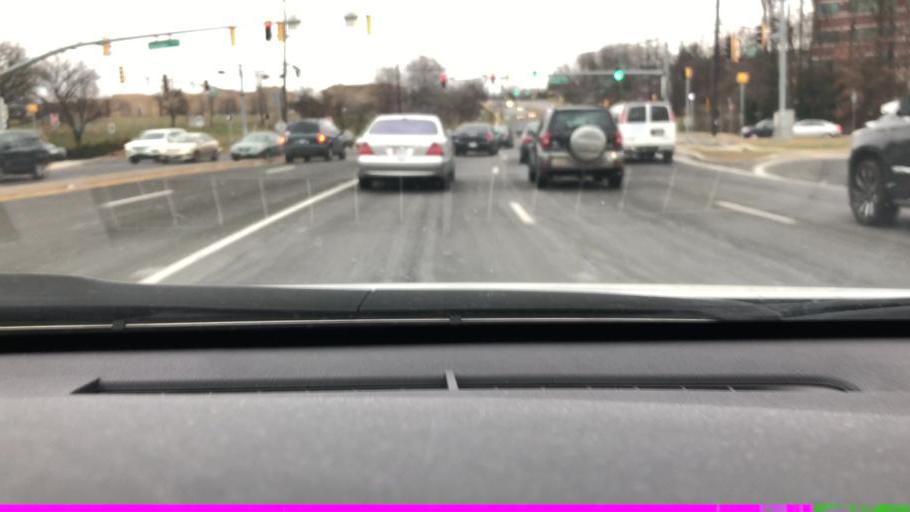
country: US
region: Maryland
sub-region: Prince George's County
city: Greenbelt
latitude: 38.9941
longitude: -76.8751
